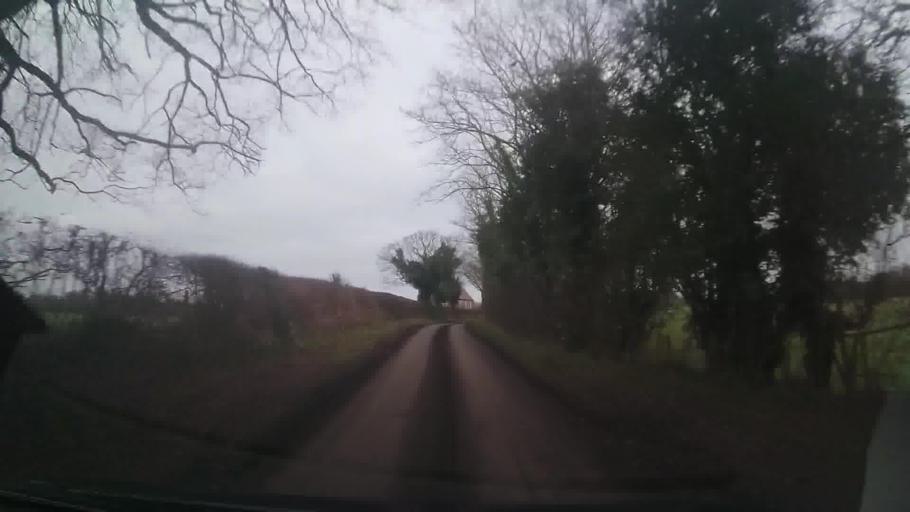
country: GB
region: England
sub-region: Shropshire
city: Wem
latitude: 52.8416
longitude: -2.7527
